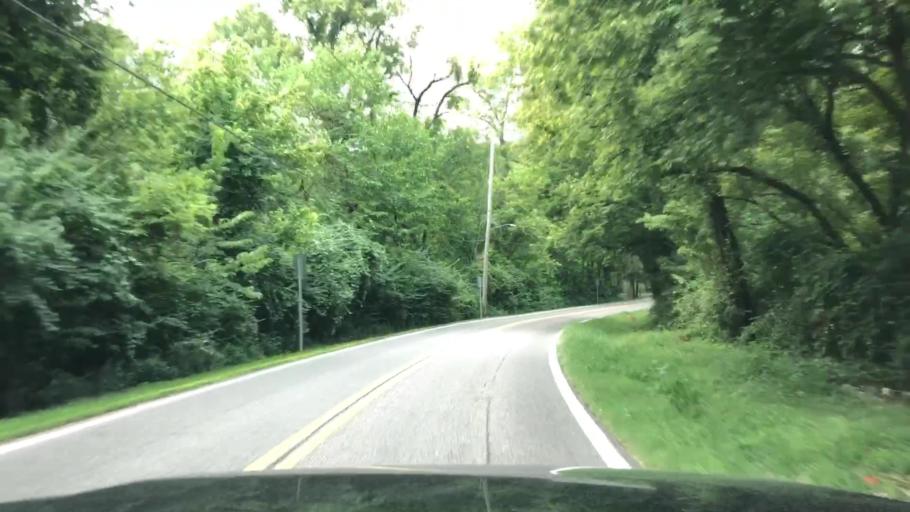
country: US
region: Missouri
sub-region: Saint Louis County
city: Hazelwood
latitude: 38.8085
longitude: -90.3821
